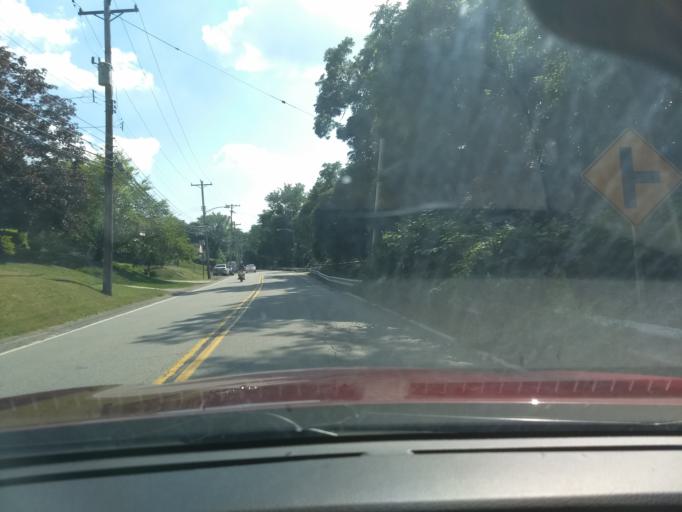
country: US
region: Pennsylvania
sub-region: Allegheny County
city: West Homestead
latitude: 40.3878
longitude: -79.9112
